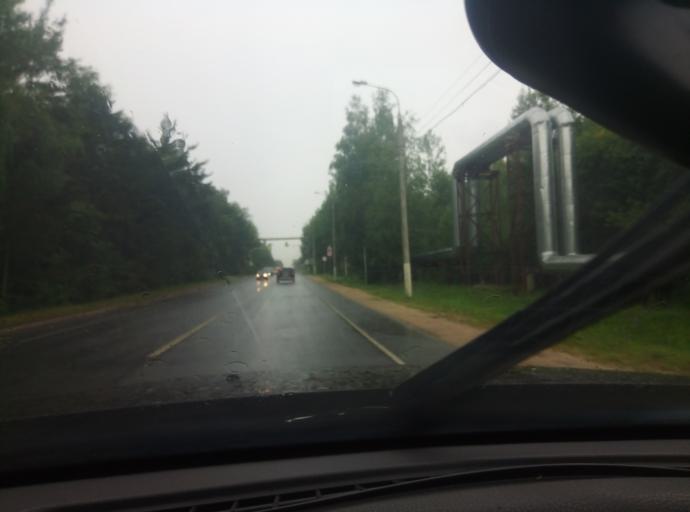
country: RU
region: Moskovskaya
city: Protvino
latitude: 54.8824
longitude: 37.2194
